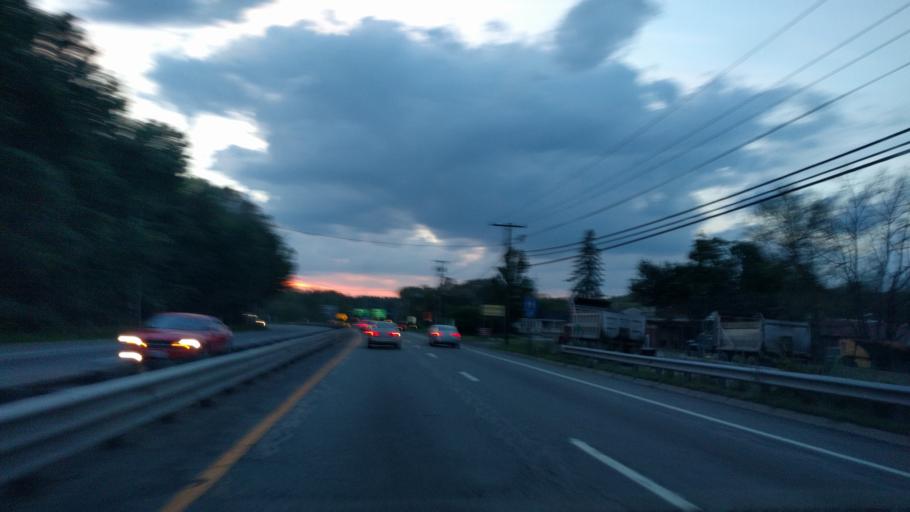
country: US
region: Rhode Island
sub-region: Providence County
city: Cumberland Hill
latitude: 41.9665
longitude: -71.5018
